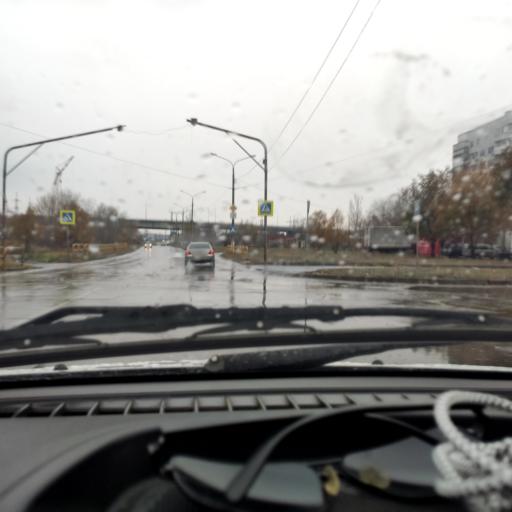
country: RU
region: Samara
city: Zhigulevsk
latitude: 53.4810
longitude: 49.5191
